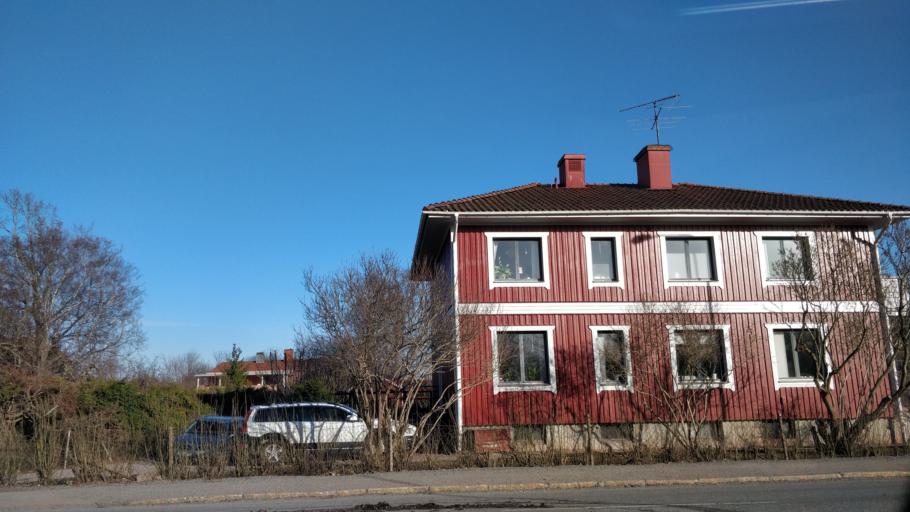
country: SE
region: Uppsala
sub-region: Enkopings Kommun
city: Orsundsbro
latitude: 59.7341
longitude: 17.3081
